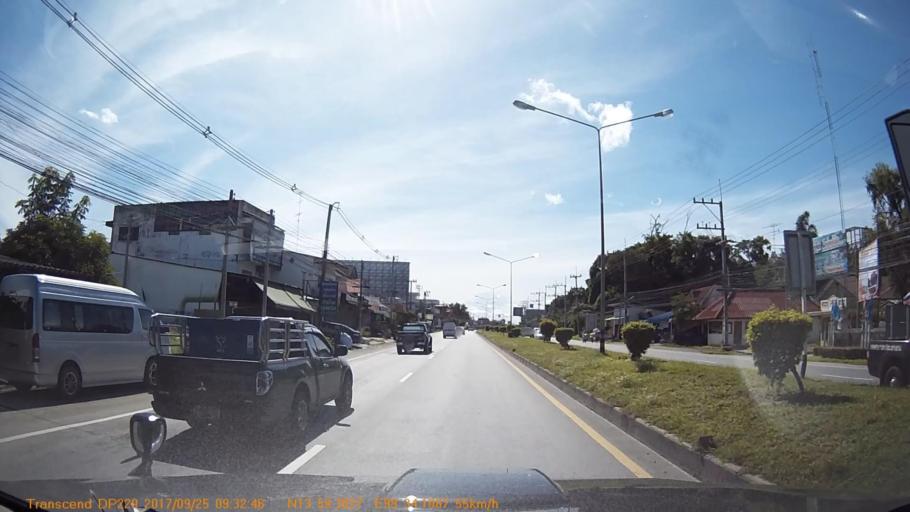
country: TH
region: Kanchanaburi
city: Kanchanaburi
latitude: 13.9896
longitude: 99.5686
